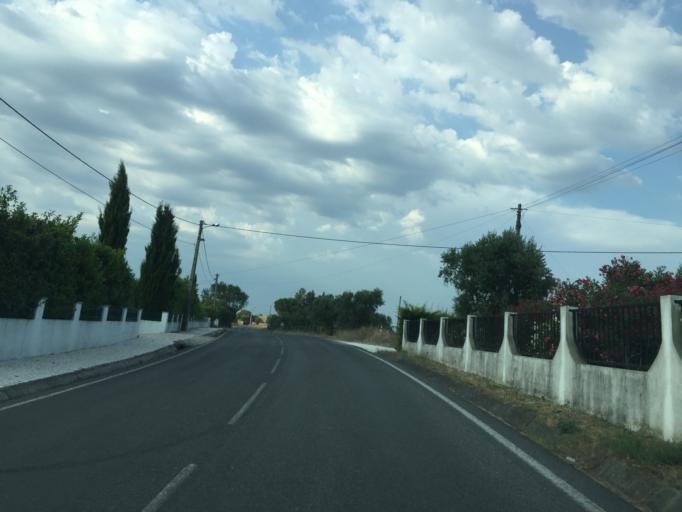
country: PT
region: Santarem
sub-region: Torres Novas
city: Torres Novas
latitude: 39.4773
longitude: -8.5776
